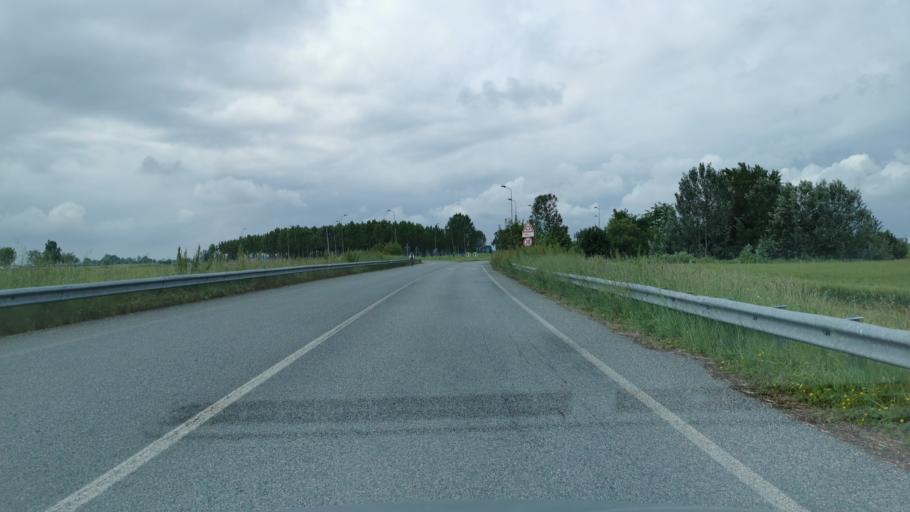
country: IT
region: Piedmont
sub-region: Provincia di Cuneo
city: Racconigi
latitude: 44.7503
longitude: 7.6917
